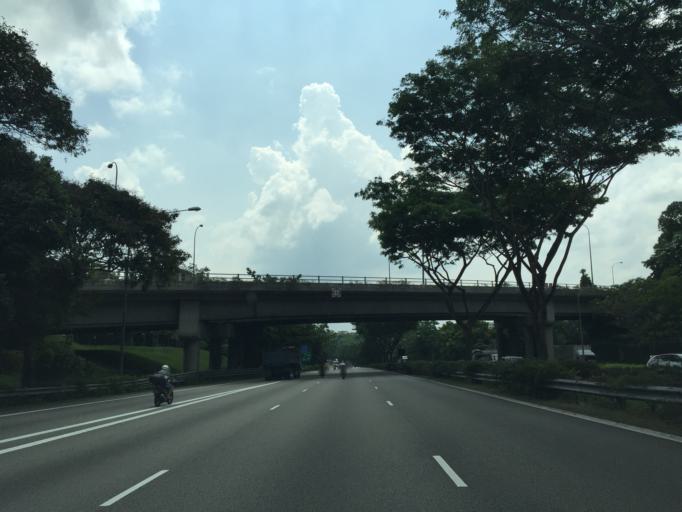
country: MY
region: Johor
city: Johor Bahru
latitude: 1.4207
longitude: 103.7712
